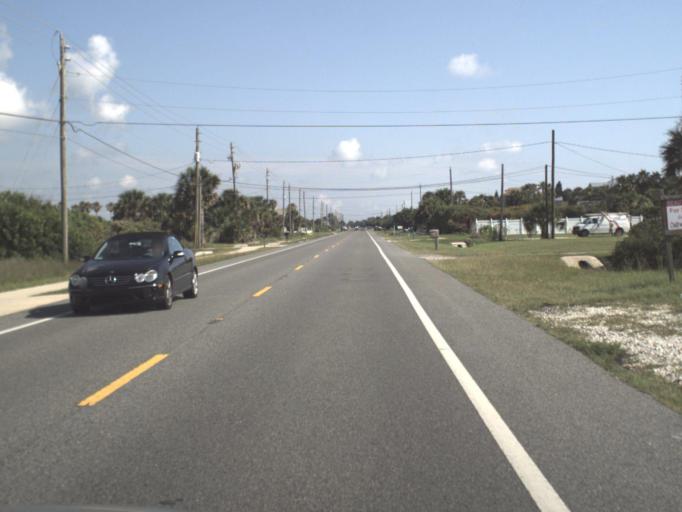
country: US
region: Florida
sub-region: Saint Johns County
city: Butler Beach
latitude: 29.7452
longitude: -81.2447
